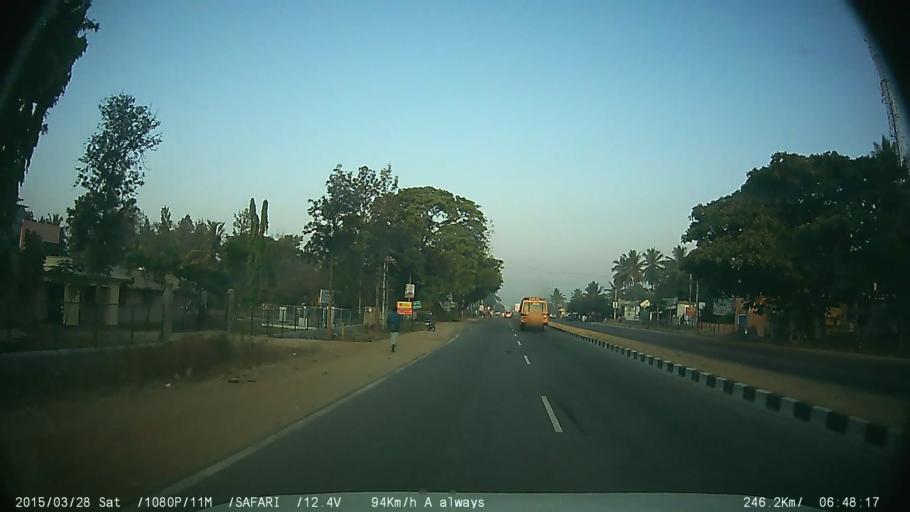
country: IN
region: Karnataka
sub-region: Mandya
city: Maddur
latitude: 12.6131
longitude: 77.0675
